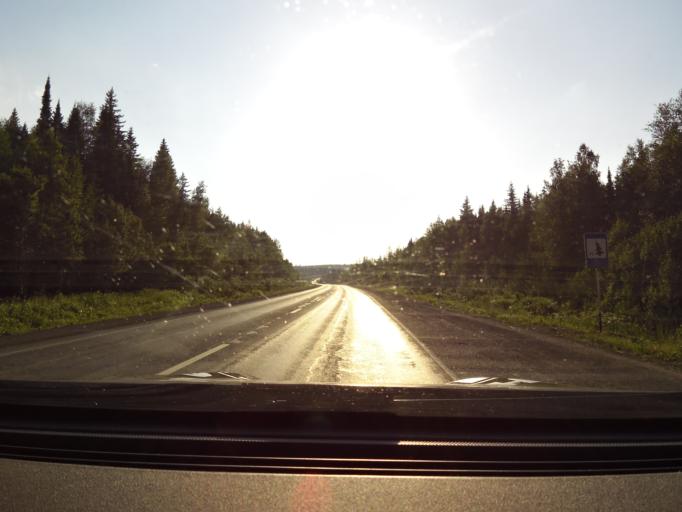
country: RU
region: Sverdlovsk
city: Bilimbay
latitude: 56.8518
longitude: 59.7997
